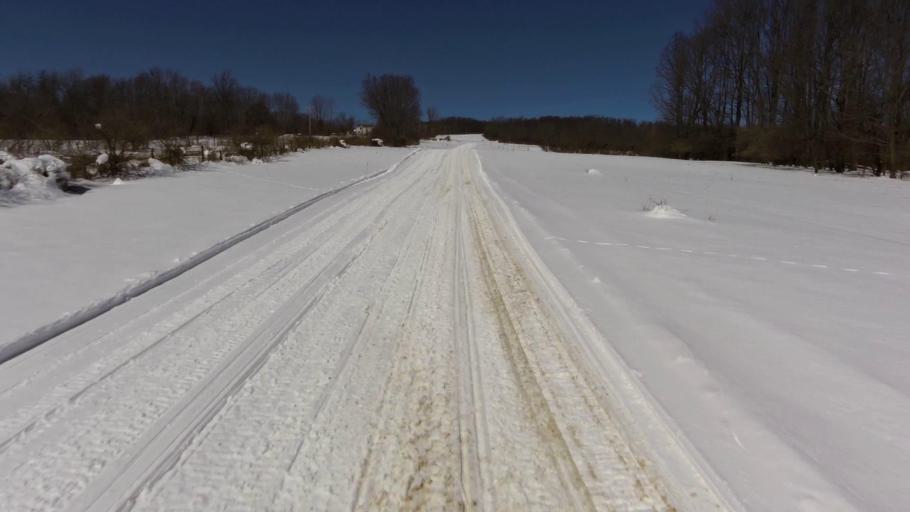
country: US
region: New York
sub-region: Allegany County
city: Cuba
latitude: 42.3426
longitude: -78.2560
